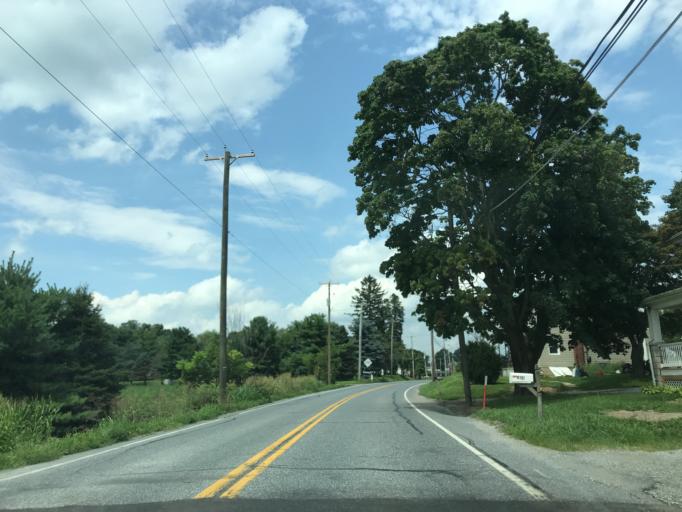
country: US
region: Pennsylvania
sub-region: York County
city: Red Lion
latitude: 39.8428
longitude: -76.6206
